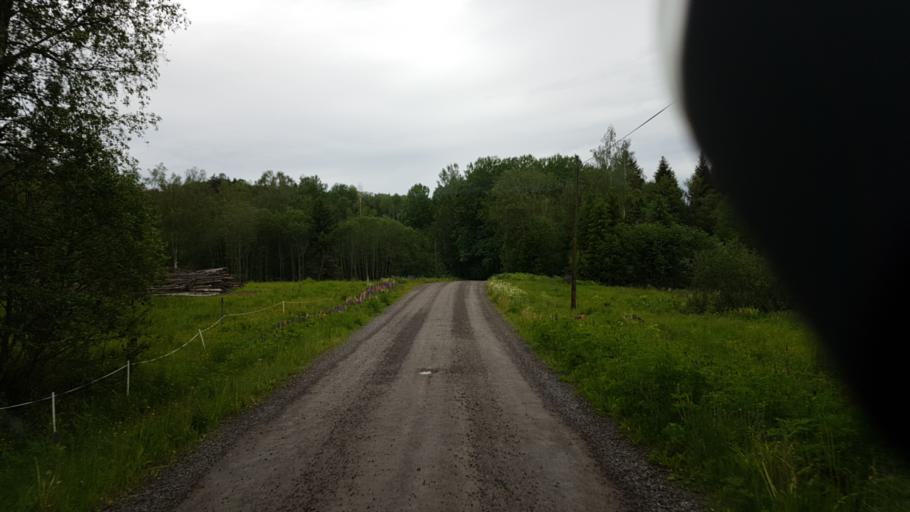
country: NO
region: Hedmark
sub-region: Eidskog
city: Skotterud
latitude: 59.7481
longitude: 12.0641
